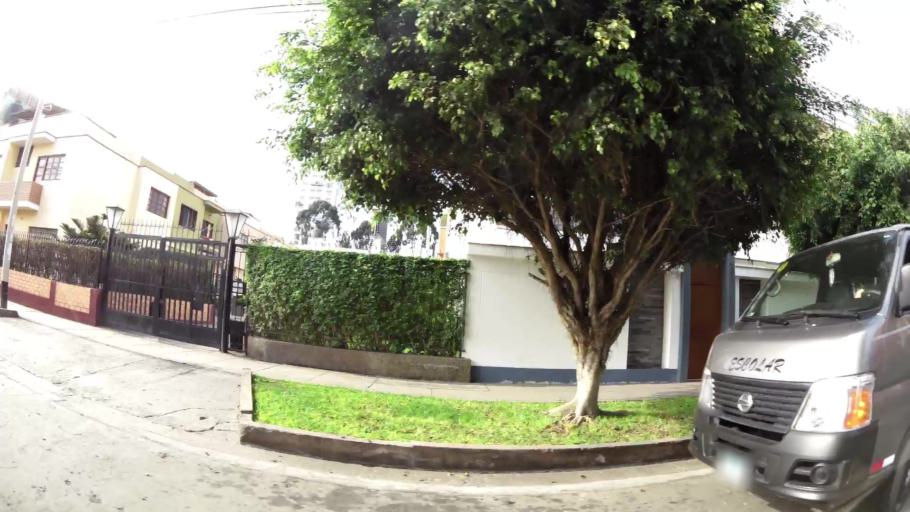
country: PE
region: Lima
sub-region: Lima
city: San Isidro
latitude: -12.0904
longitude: -77.0594
